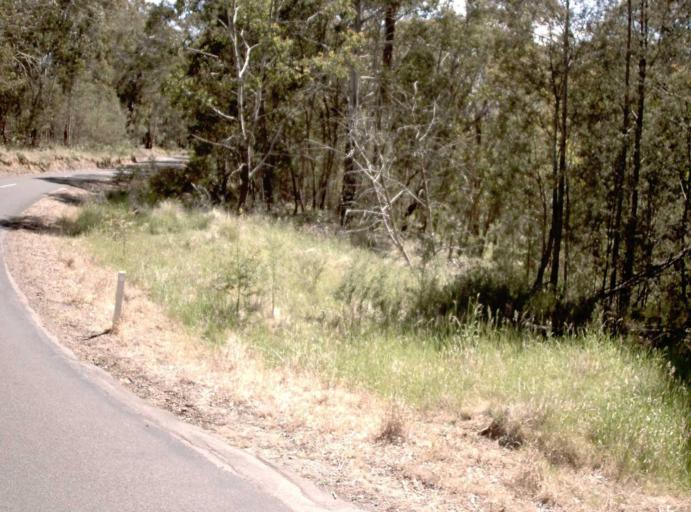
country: AU
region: New South Wales
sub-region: Bombala
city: Bombala
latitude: -37.0658
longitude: 148.7975
